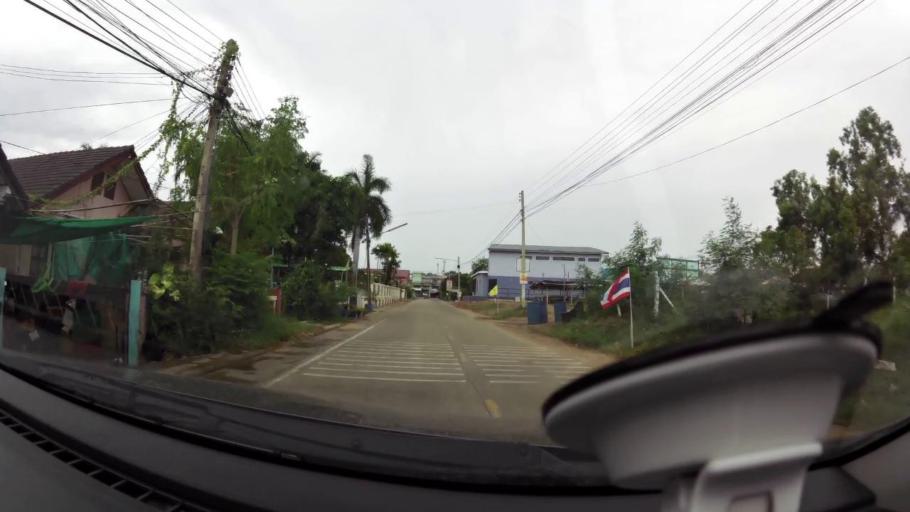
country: TH
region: Prachuap Khiri Khan
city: Pran Buri
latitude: 12.3907
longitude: 99.9847
